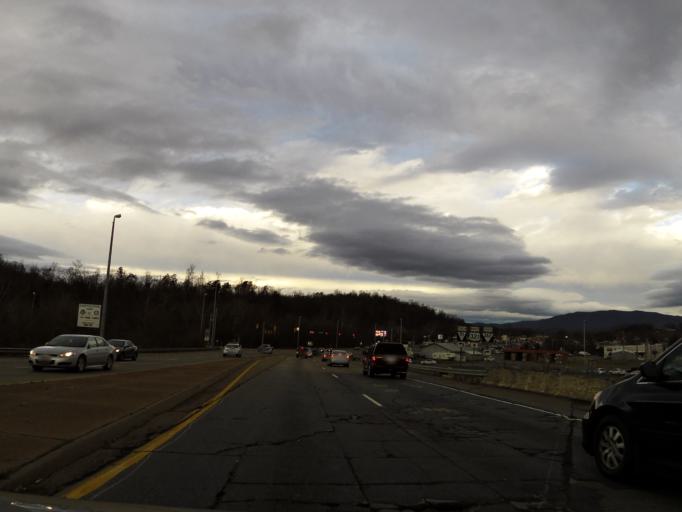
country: US
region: Tennessee
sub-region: Carter County
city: Central
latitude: 36.3275
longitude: -82.2700
